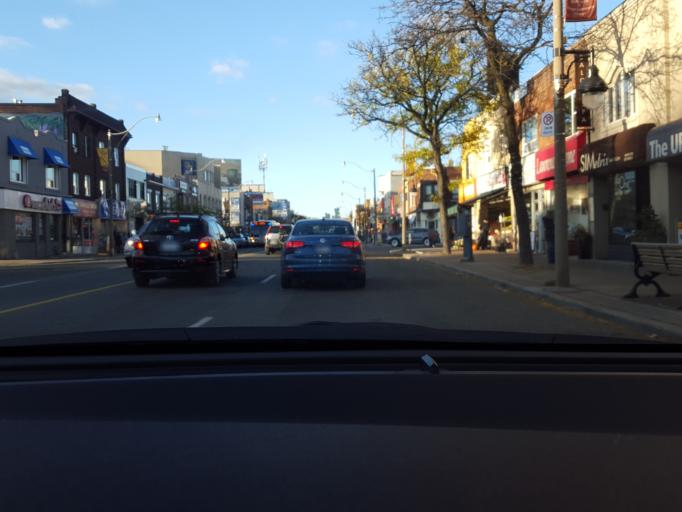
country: CA
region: Ontario
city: Toronto
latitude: 43.7282
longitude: -79.4030
